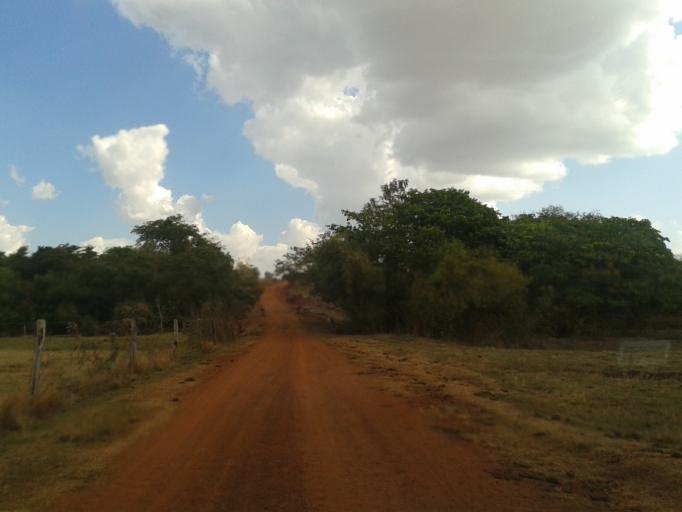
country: BR
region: Minas Gerais
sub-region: Santa Vitoria
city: Santa Vitoria
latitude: -19.2471
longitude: -49.9778
